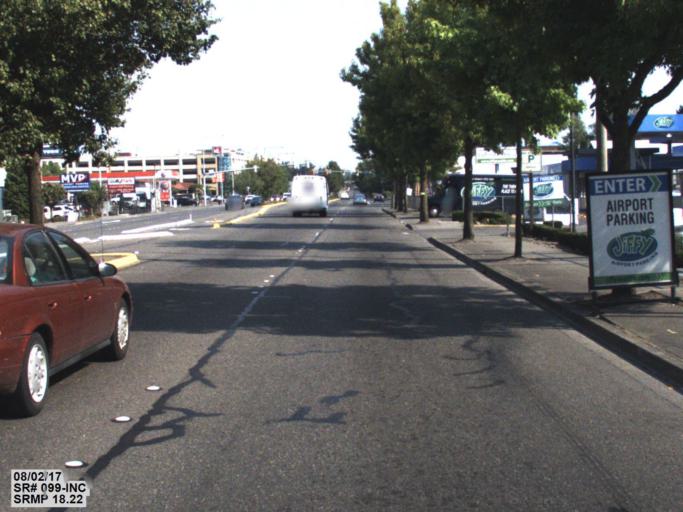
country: US
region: Washington
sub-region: King County
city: SeaTac
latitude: 47.4327
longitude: -122.2953
